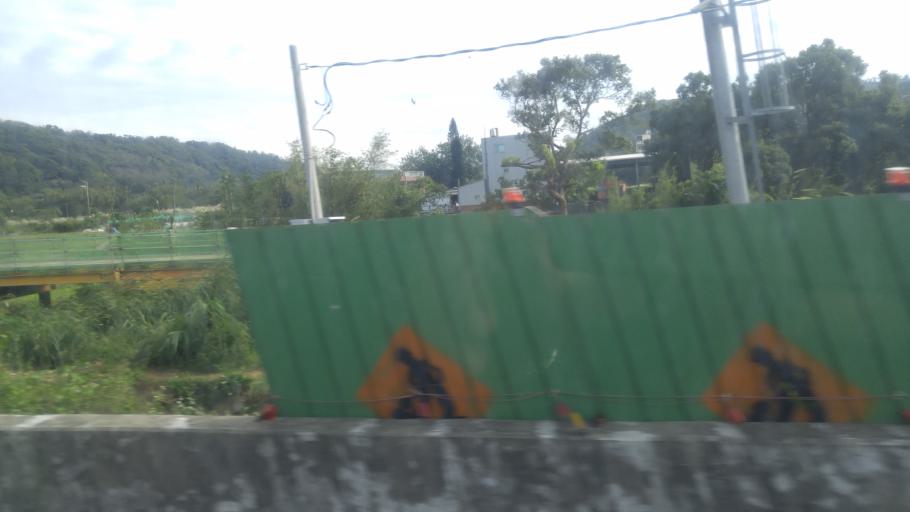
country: TW
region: Taiwan
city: Daxi
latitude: 24.9004
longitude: 121.1518
